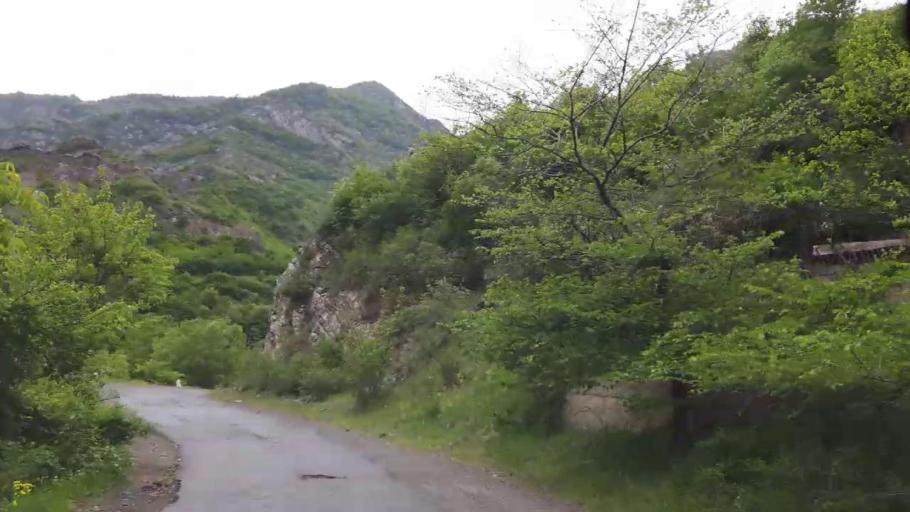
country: GE
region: Shida Kartli
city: Gori
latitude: 41.9014
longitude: 44.0911
